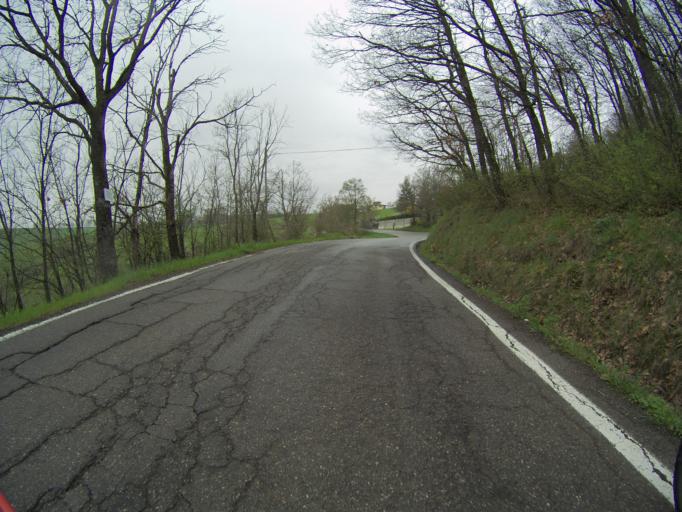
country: IT
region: Emilia-Romagna
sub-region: Provincia di Reggio Emilia
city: Ciano d'Enza
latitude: 44.5451
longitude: 10.4169
